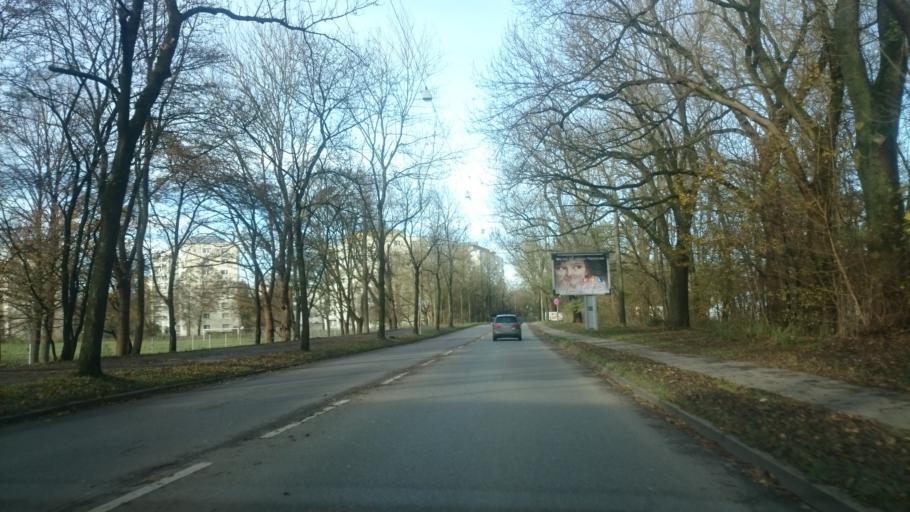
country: DE
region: Bavaria
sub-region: Swabia
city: Augsburg
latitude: 48.3582
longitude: 10.9333
